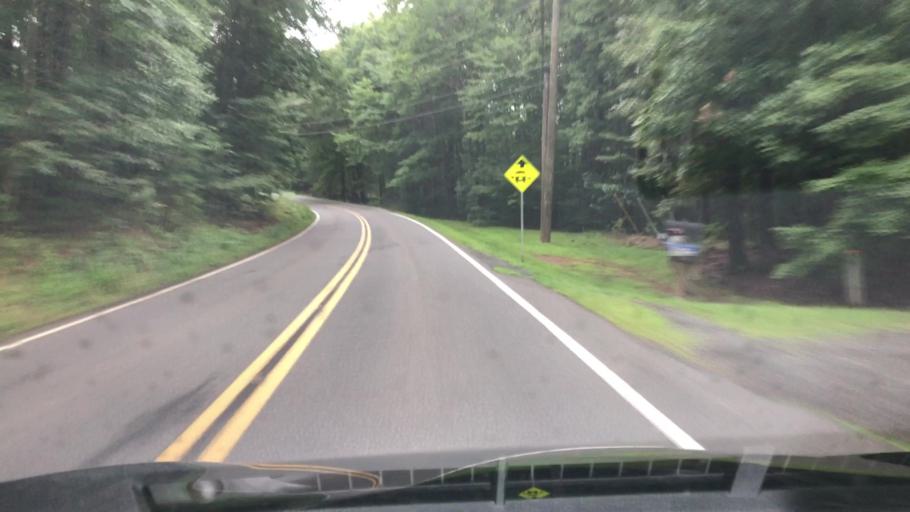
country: US
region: Virginia
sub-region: Prince William County
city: Nokesville
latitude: 38.5710
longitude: -77.6176
